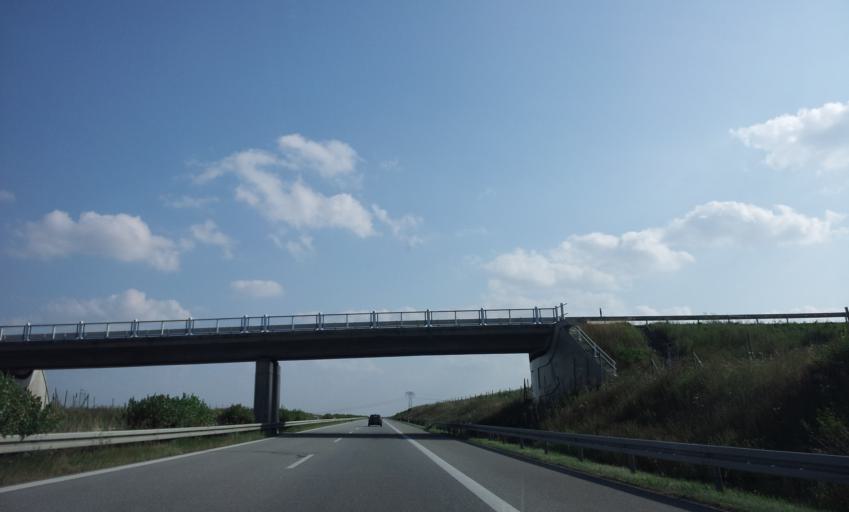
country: DE
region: Mecklenburg-Vorpommern
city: Burow
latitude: 53.8235
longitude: 13.3246
